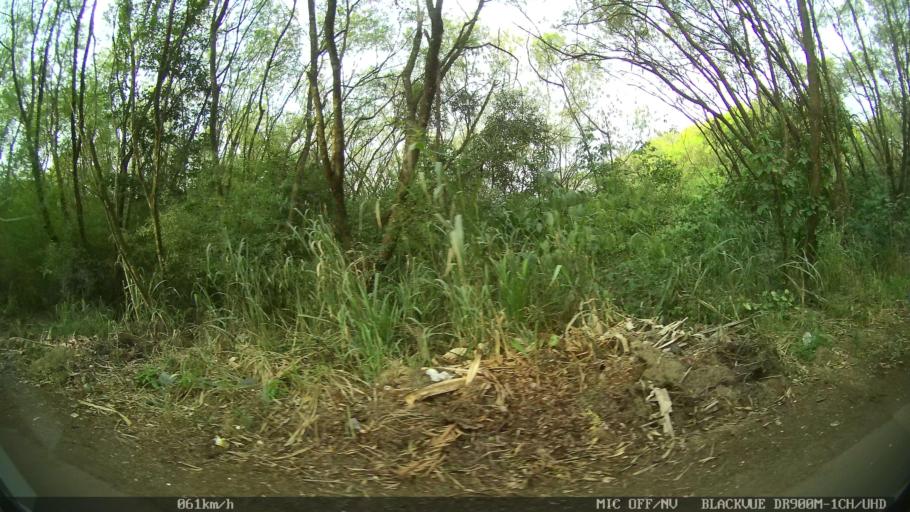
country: BR
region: Sao Paulo
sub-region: Piracicaba
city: Piracicaba
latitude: -22.6995
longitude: -47.5881
